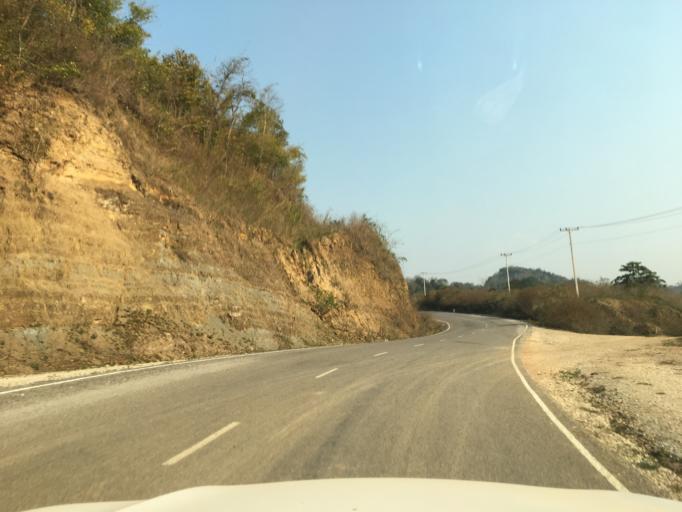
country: LA
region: Houaphan
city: Xam Nua
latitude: 20.5701
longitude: 104.0502
